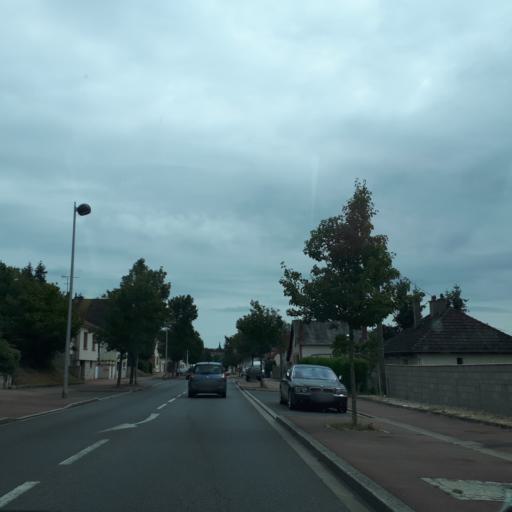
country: FR
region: Centre
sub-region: Departement du Loiret
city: Gien
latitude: 47.6943
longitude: 2.6144
